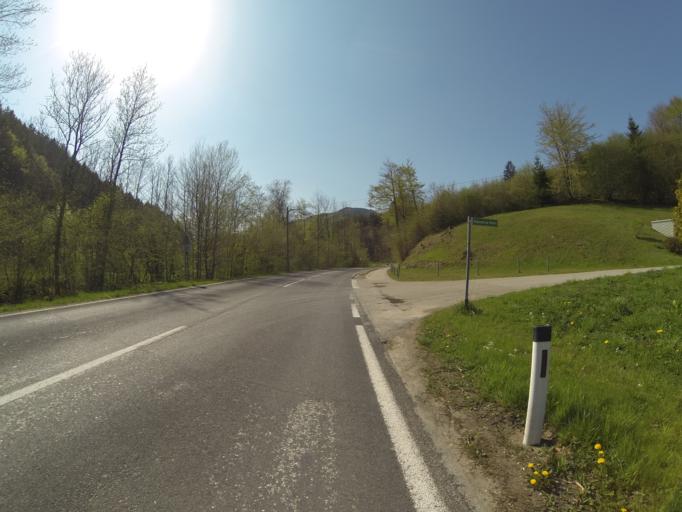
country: AT
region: Upper Austria
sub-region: Politischer Bezirk Gmunden
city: Altmunster
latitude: 47.9223
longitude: 13.7447
